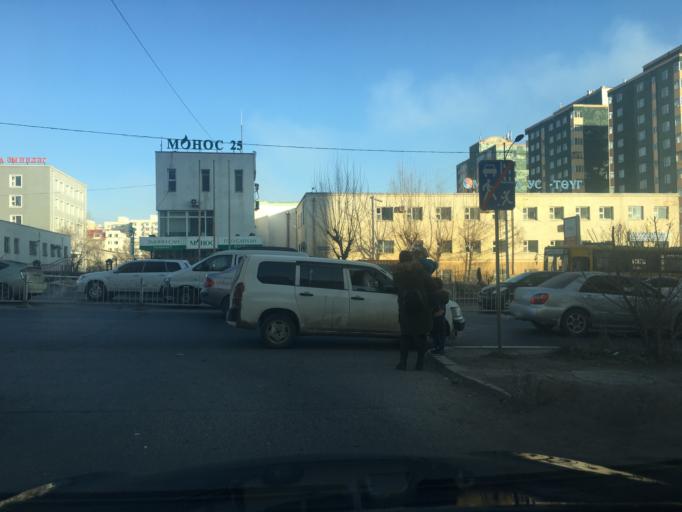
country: MN
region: Ulaanbaatar
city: Ulaanbaatar
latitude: 47.9156
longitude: 106.8762
